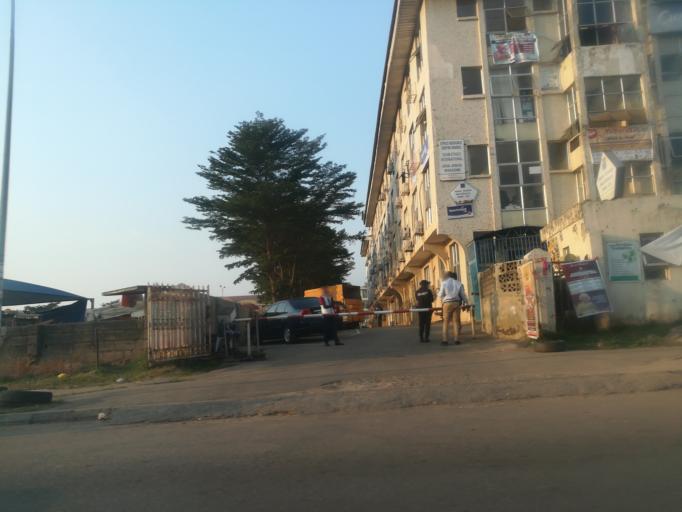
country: NG
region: Abuja Federal Capital Territory
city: Abuja
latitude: 9.0666
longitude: 7.4403
